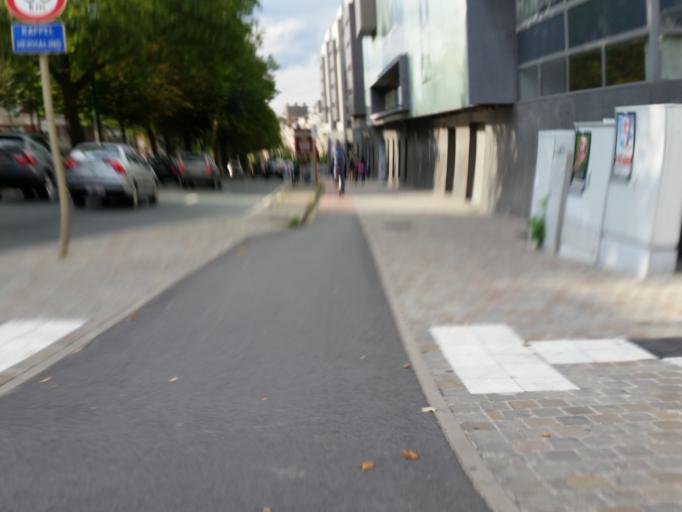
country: BE
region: Brussels Capital
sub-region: Bruxelles-Capitale
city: Brussels
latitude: 50.8692
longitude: 4.3849
